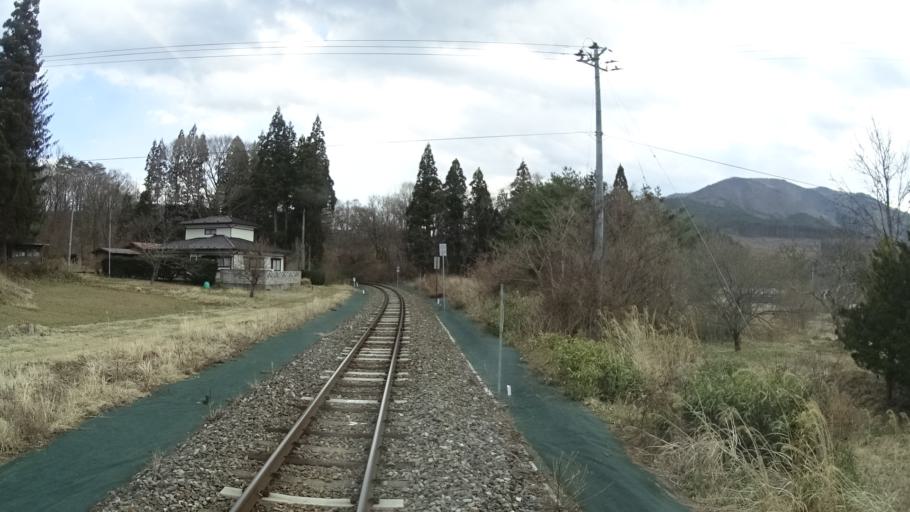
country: JP
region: Iwate
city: Tono
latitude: 39.3047
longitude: 141.3798
